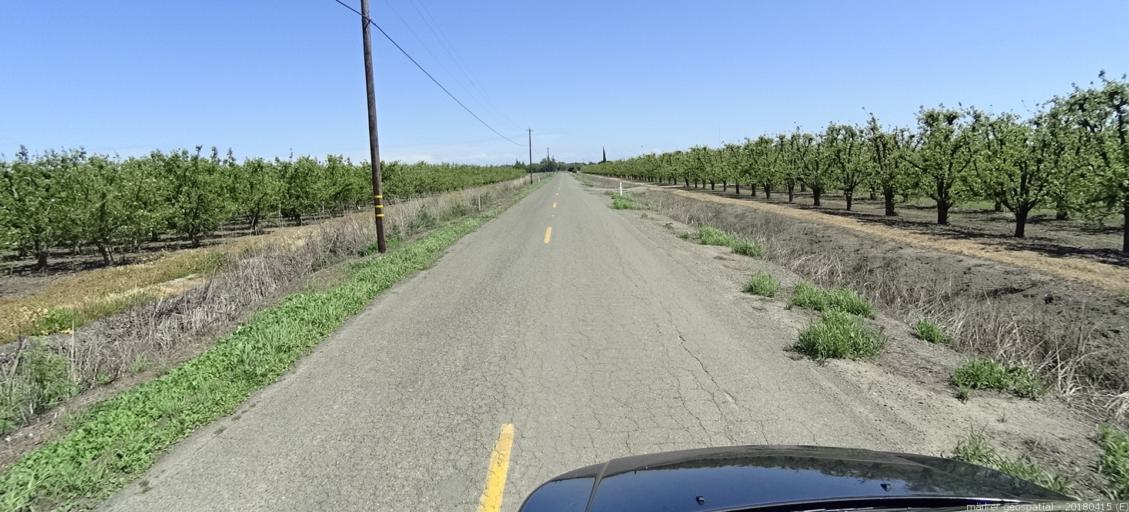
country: US
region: California
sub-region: Sacramento County
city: Walnut Grove
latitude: 38.2958
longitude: -121.6009
